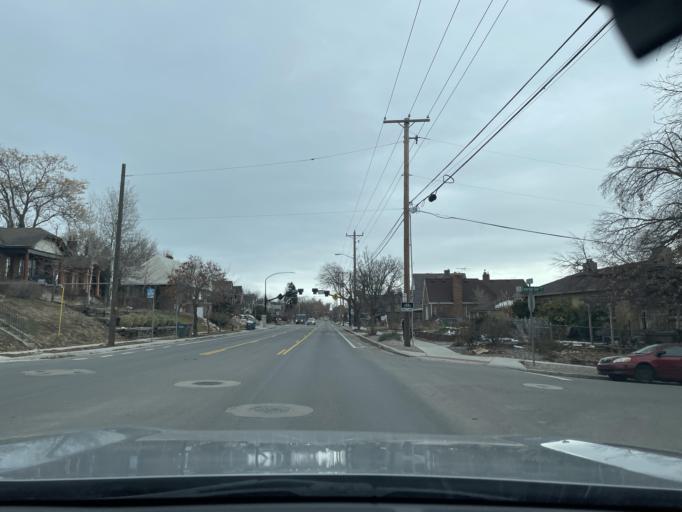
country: US
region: Utah
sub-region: Salt Lake County
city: Willard
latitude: 40.7373
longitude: -111.8538
